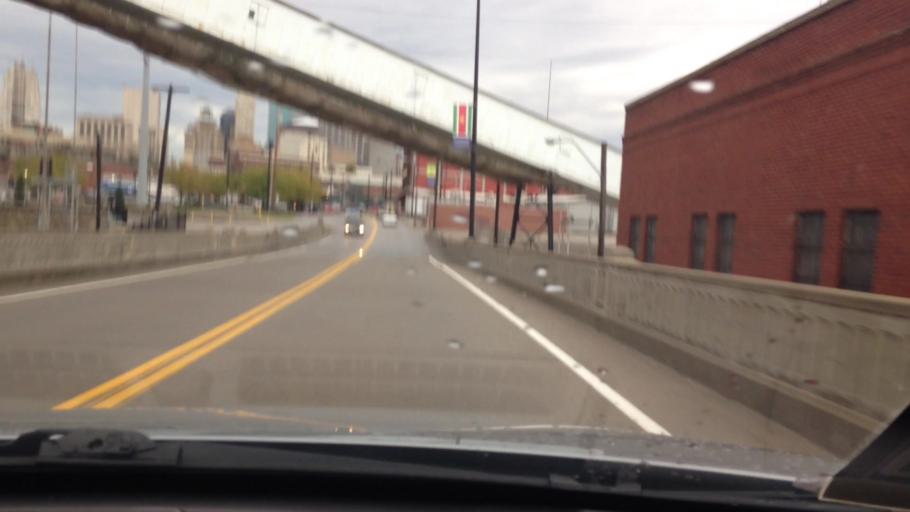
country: US
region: Missouri
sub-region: Jackson County
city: Kansas City
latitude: 39.1126
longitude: -94.5807
